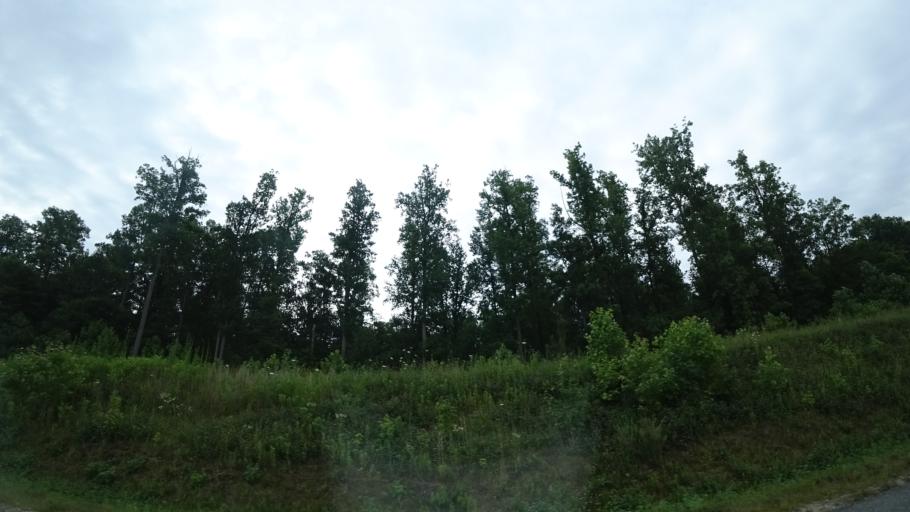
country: US
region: Virginia
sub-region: Spotsylvania County
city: Spotsylvania Courthouse
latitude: 38.1647
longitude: -77.6392
